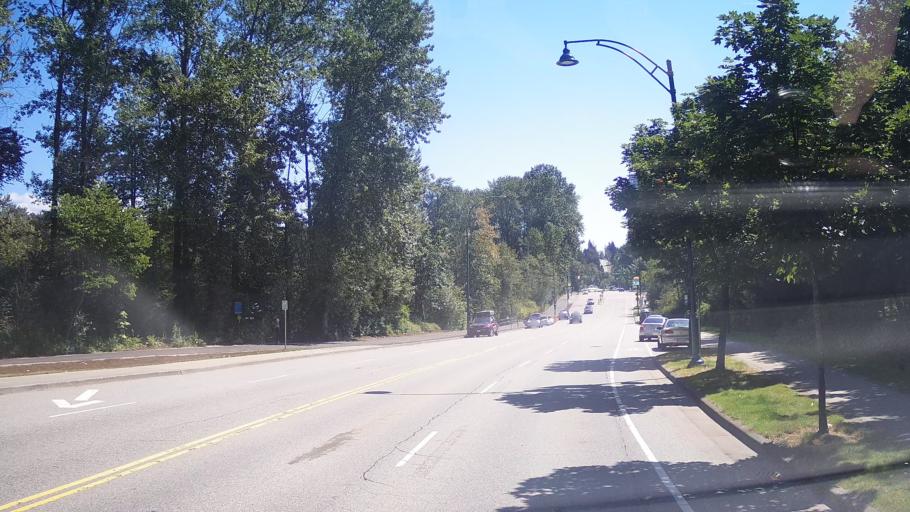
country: CA
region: British Columbia
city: Port Moody
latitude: 49.2804
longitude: -122.8369
